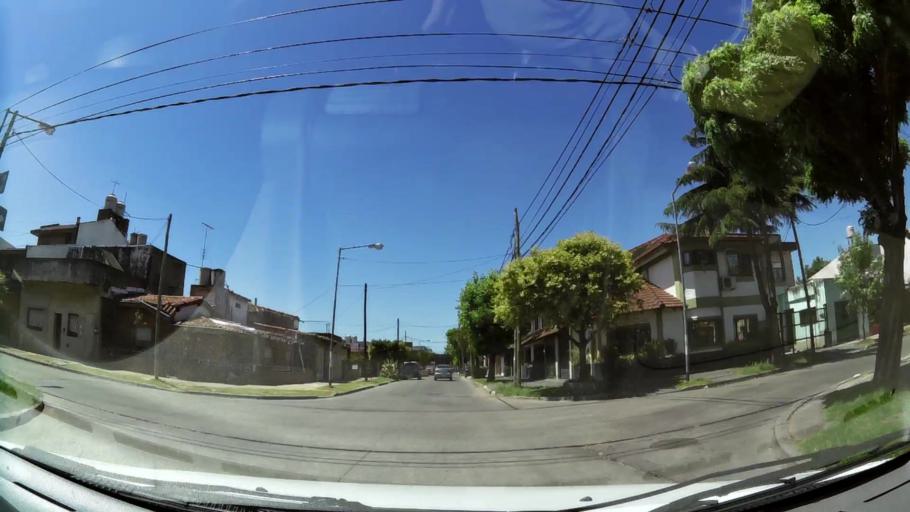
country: AR
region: Buenos Aires
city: Caseros
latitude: -34.5842
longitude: -58.5687
